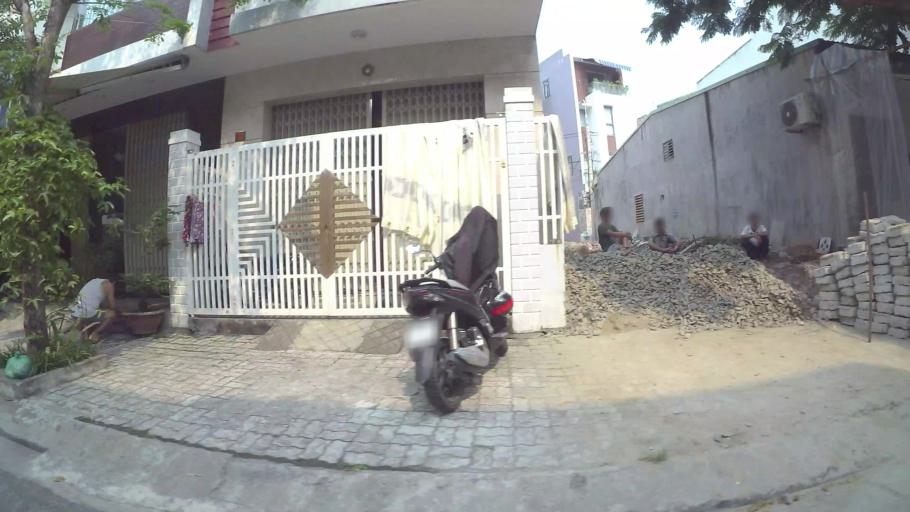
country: VN
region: Da Nang
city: Cam Le
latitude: 16.0418
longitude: 108.2141
